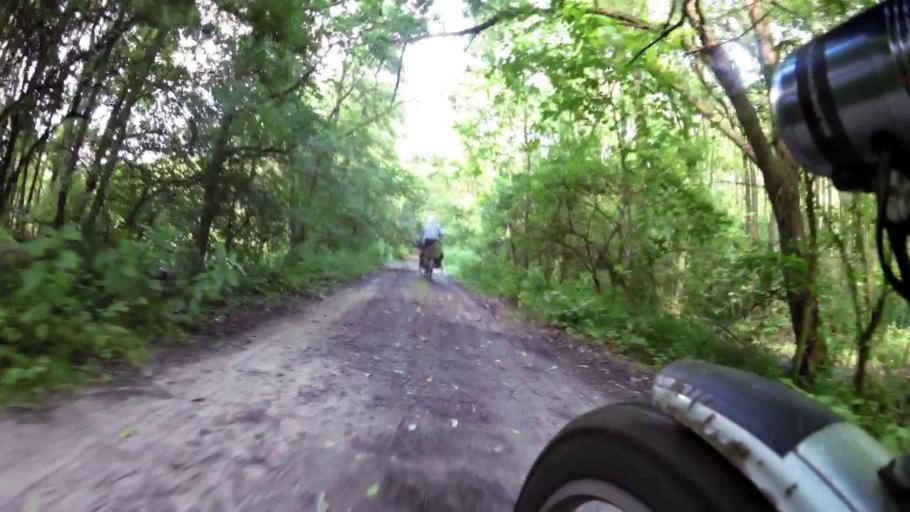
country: PL
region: West Pomeranian Voivodeship
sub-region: Powiat swidwinski
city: Swidwin
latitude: 53.7350
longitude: 15.7536
